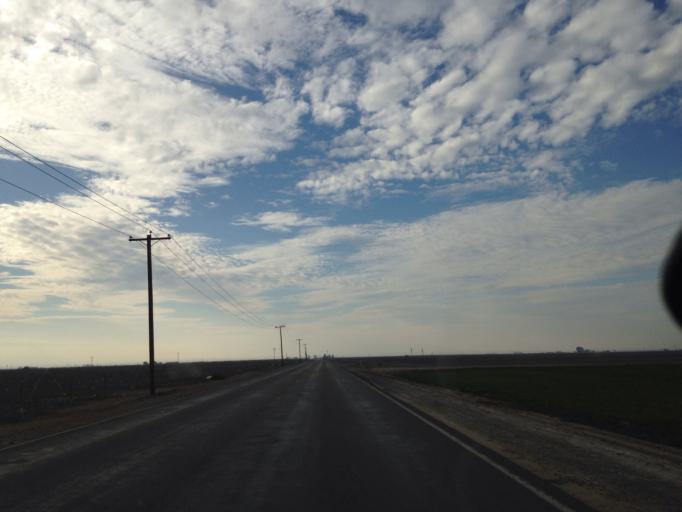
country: US
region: California
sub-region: Kern County
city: Buttonwillow
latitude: 35.4424
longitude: -119.4957
